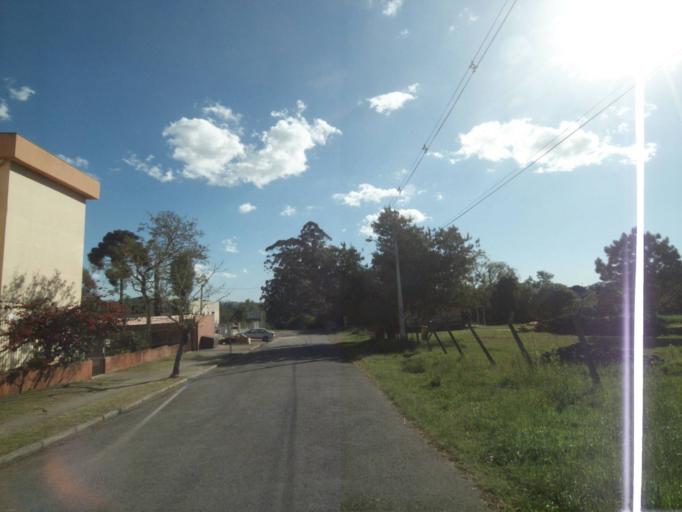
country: BR
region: Parana
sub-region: Curitiba
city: Curitiba
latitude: -25.3848
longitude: -49.2387
